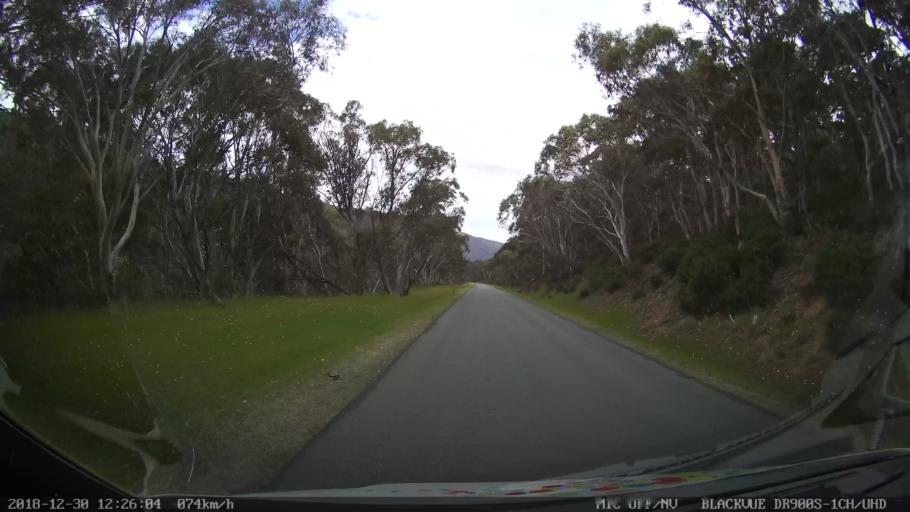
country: AU
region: New South Wales
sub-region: Snowy River
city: Jindabyne
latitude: -36.3434
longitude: 148.4890
